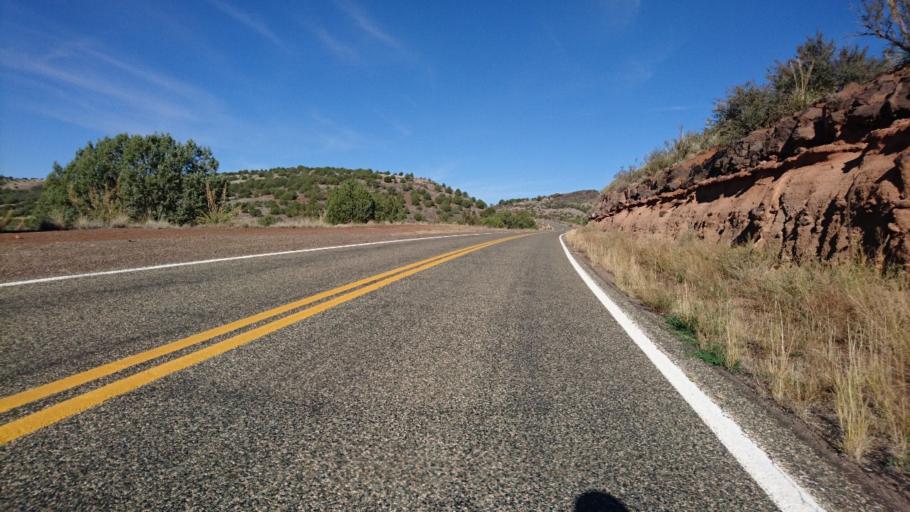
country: US
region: Arizona
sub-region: Yavapai County
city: Paulden
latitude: 35.2743
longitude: -112.6883
